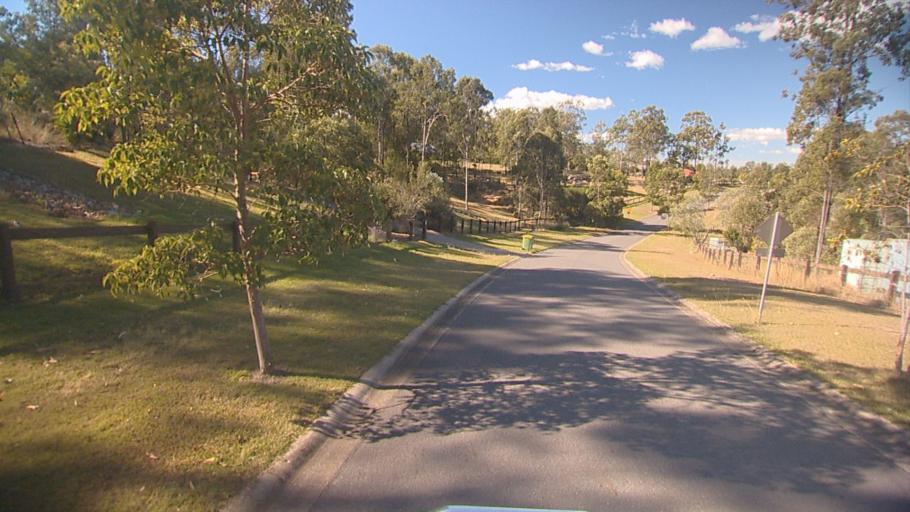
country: AU
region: Queensland
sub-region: Ipswich
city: Springfield Lakes
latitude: -27.7228
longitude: 152.9256
